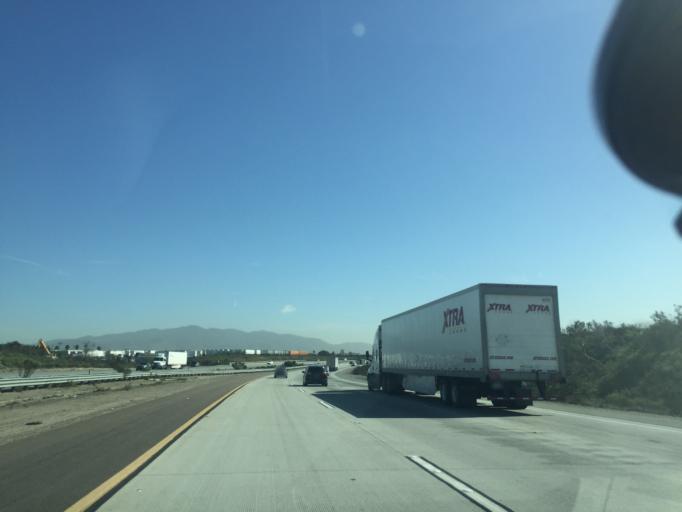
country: MX
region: Baja California
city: Tijuana
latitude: 32.5663
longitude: -117.0067
